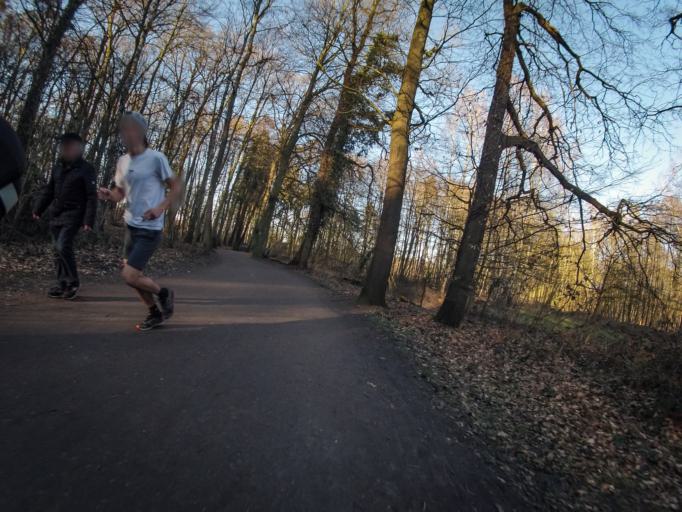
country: DE
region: Lower Saxony
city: Osnabrueck
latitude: 52.2895
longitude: 7.9847
